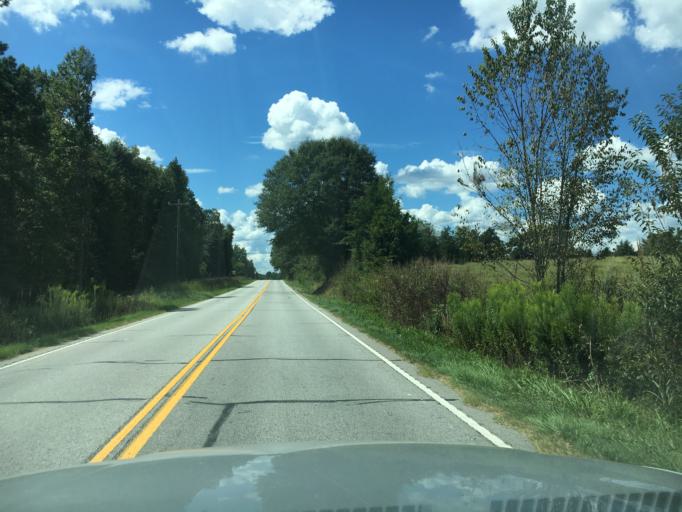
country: US
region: South Carolina
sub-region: Greenwood County
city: Ware Shoals
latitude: 34.5194
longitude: -82.1688
